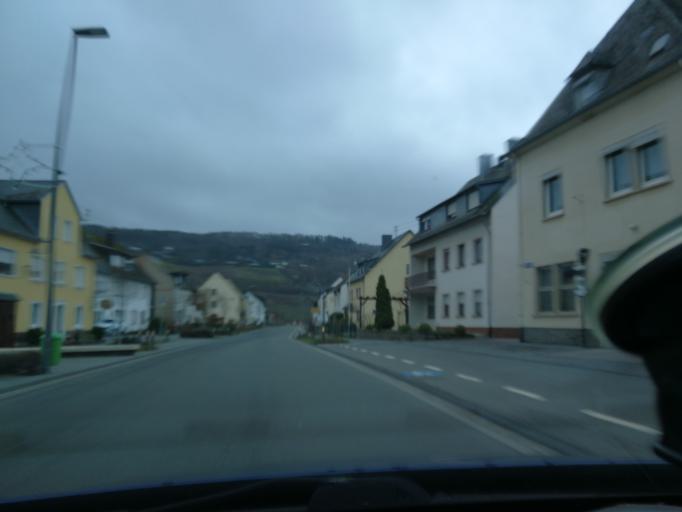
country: DE
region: Rheinland-Pfalz
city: Trittenheim
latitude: 49.8204
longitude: 6.8989
